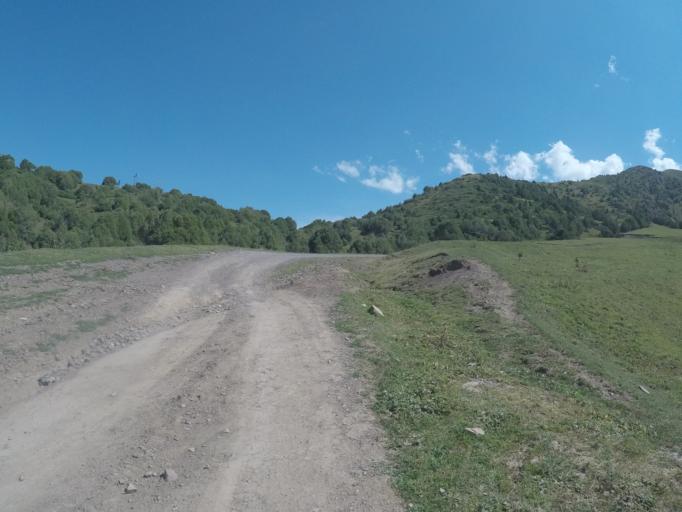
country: KG
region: Chuy
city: Bishkek
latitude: 42.6477
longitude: 74.5583
